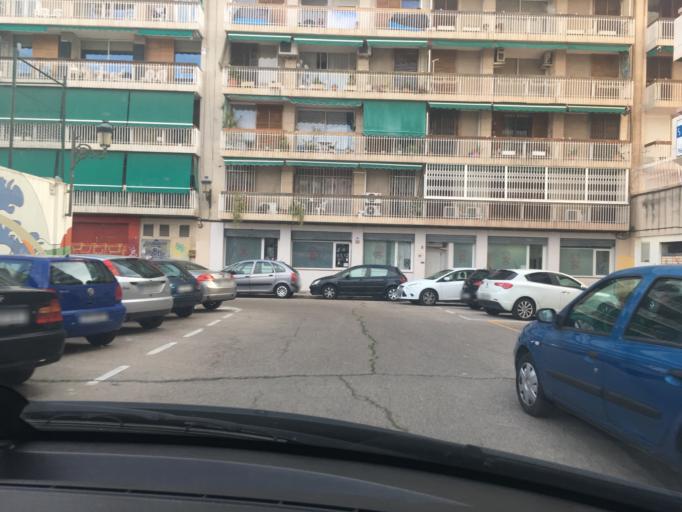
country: ES
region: Valencia
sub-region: Provincia de Valencia
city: Valencia
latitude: 39.4729
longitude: -0.3918
